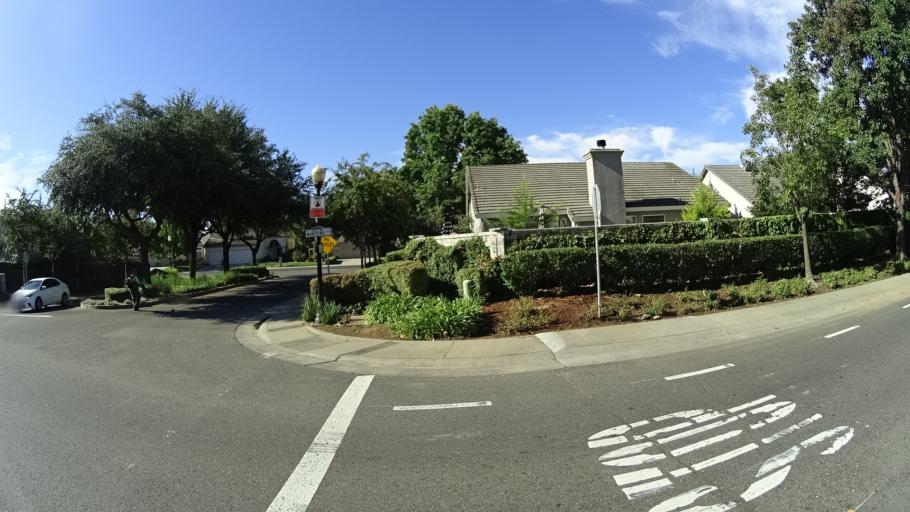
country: US
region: California
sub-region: Sacramento County
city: Laguna
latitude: 38.4063
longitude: -121.4696
